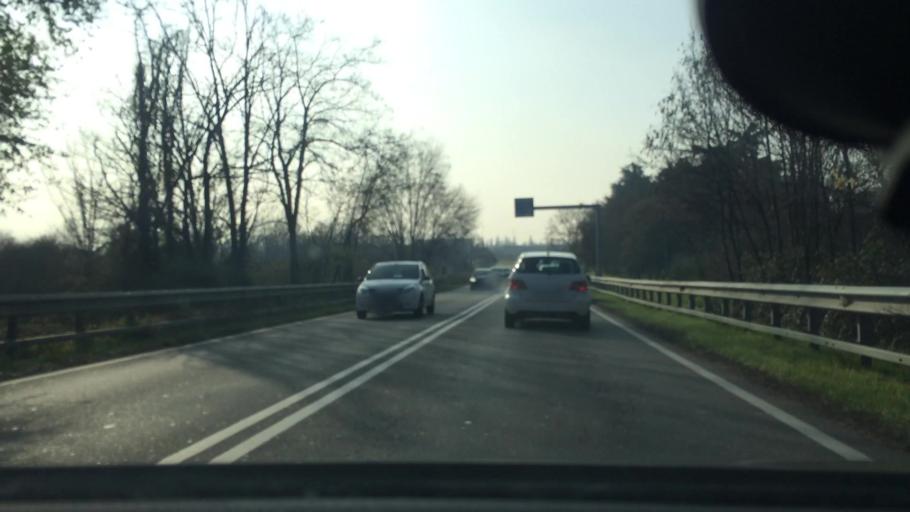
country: IT
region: Lombardy
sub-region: Citta metropolitana di Milano
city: Garbagnate Milanese
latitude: 45.5684
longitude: 9.0880
